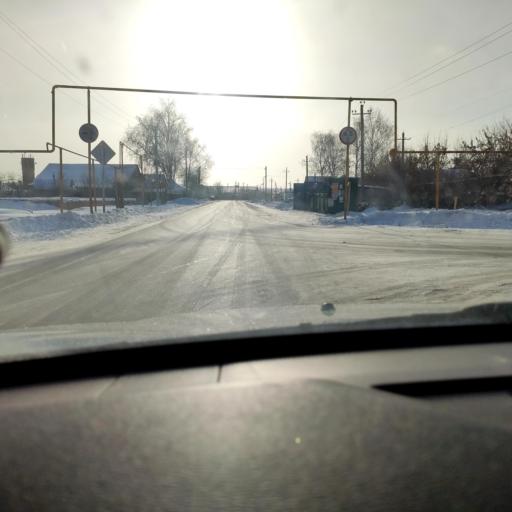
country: RU
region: Samara
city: Smyshlyayevka
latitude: 53.1623
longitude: 50.3827
